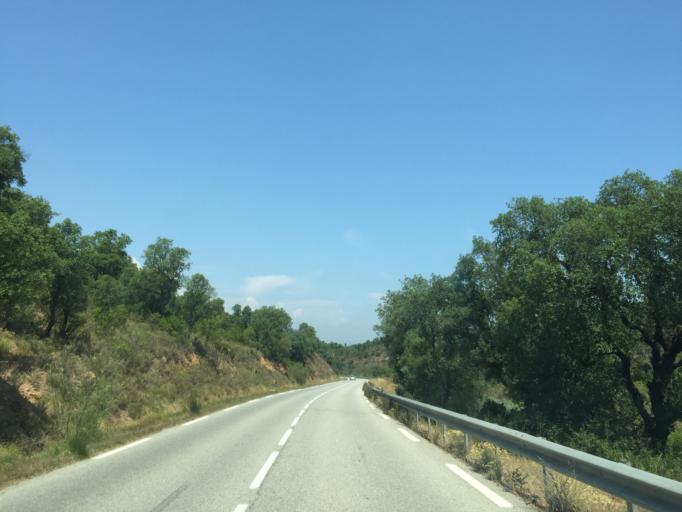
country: FR
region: Provence-Alpes-Cote d'Azur
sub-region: Departement du Var
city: Roquebrune-sur-Argens
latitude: 43.3751
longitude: 6.6739
